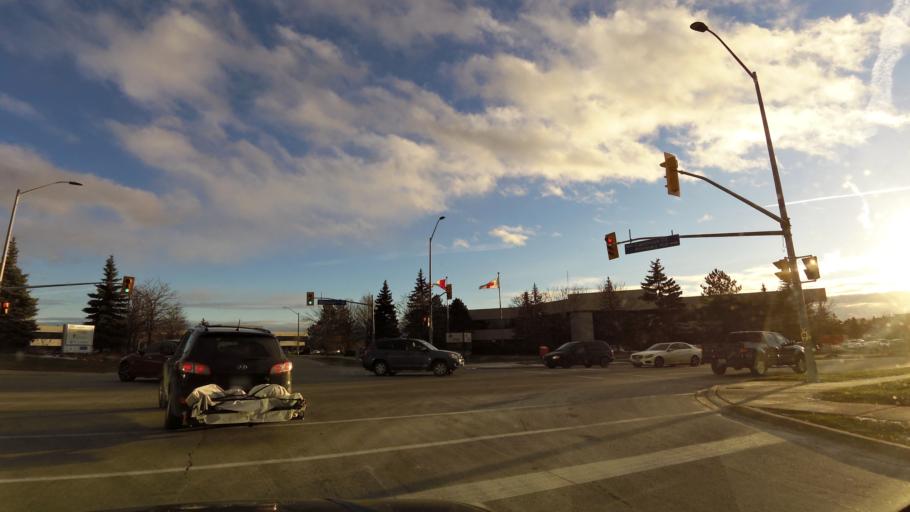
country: CA
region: Ontario
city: Mississauga
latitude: 43.6162
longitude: -79.6755
